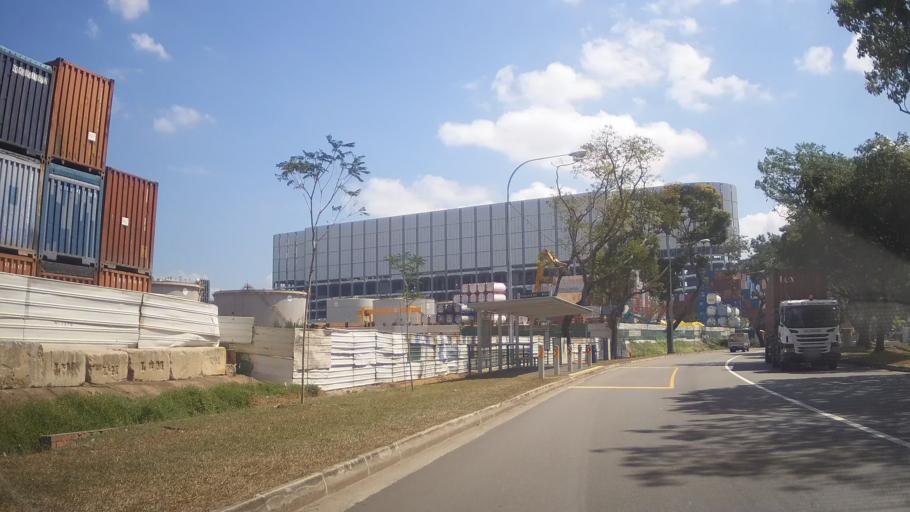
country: SG
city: Singapore
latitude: 1.3072
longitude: 103.6937
